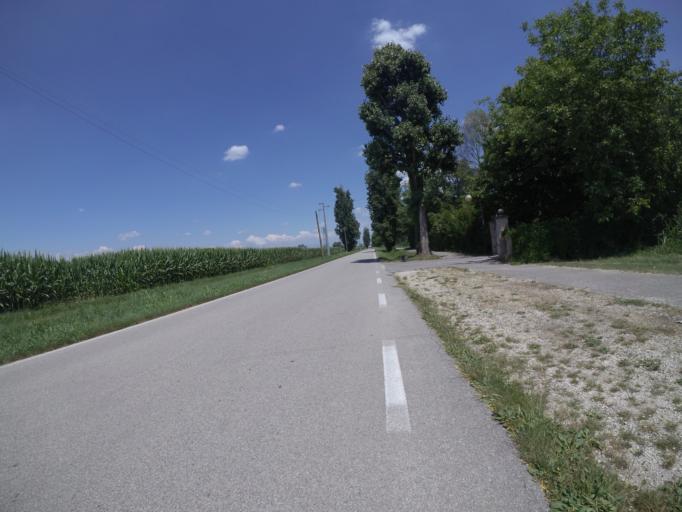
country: IT
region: Friuli Venezia Giulia
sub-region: Provincia di Udine
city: Varmo
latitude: 45.9238
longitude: 12.9985
